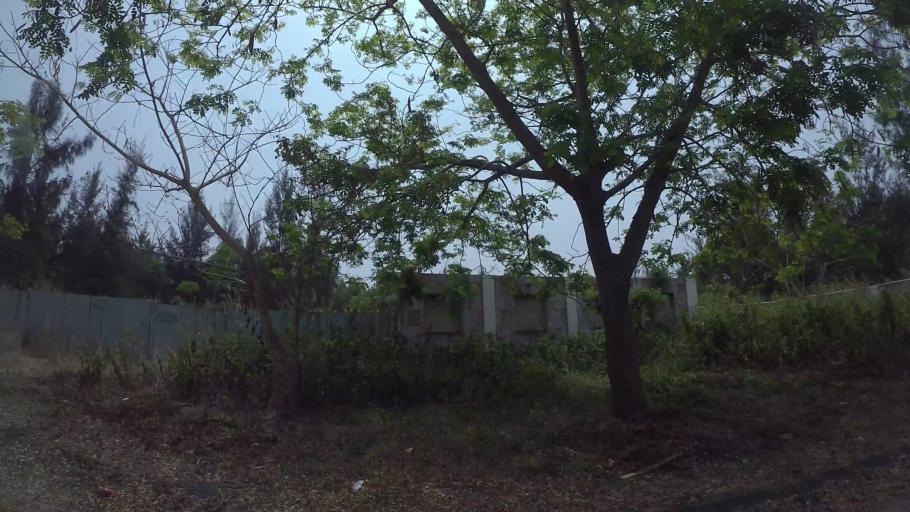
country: VN
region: Da Nang
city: Son Tra
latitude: 16.0969
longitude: 108.2682
